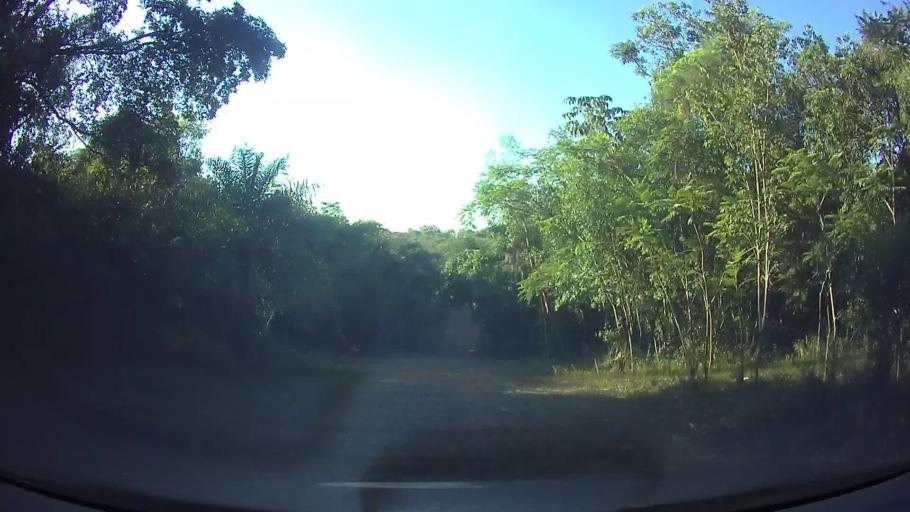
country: PY
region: Cordillera
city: San Bernardino
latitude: -25.3107
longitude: -57.2659
